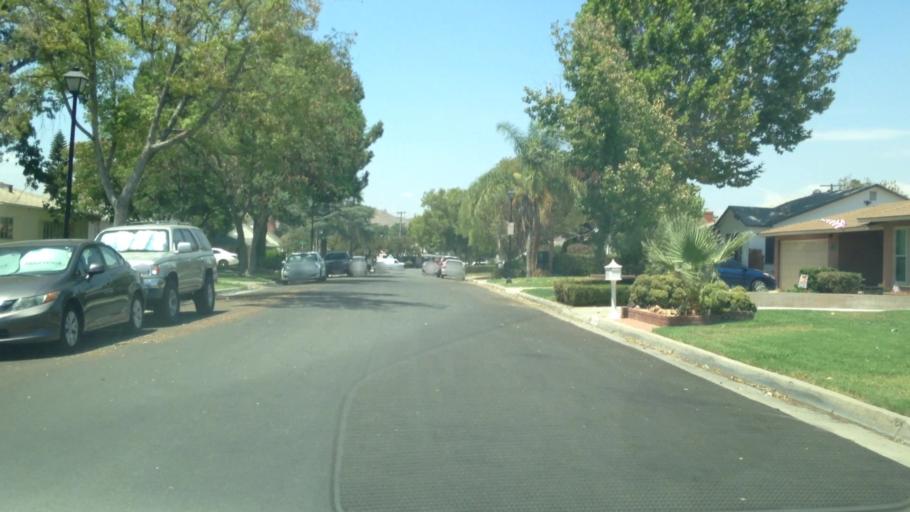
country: US
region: California
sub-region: Riverside County
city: Riverside
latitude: 33.9591
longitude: -117.3906
